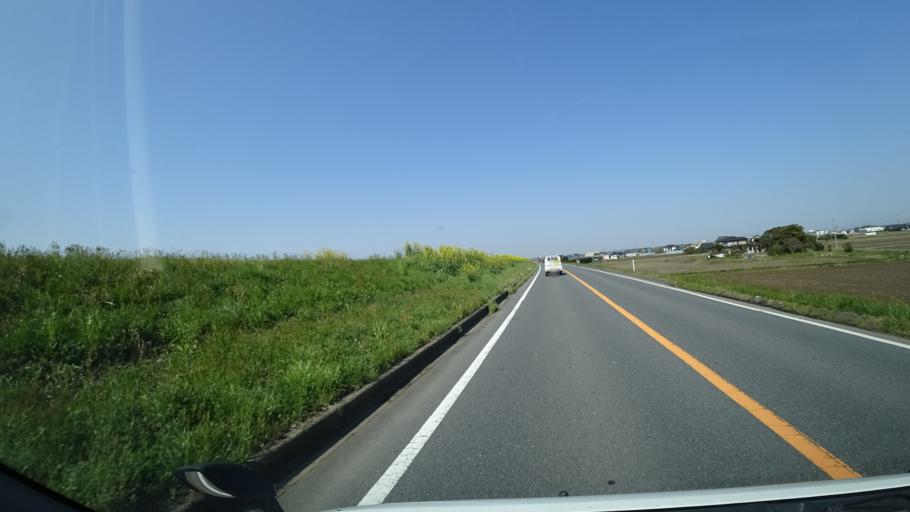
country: JP
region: Chiba
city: Katori-shi
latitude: 35.9195
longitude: 140.4689
